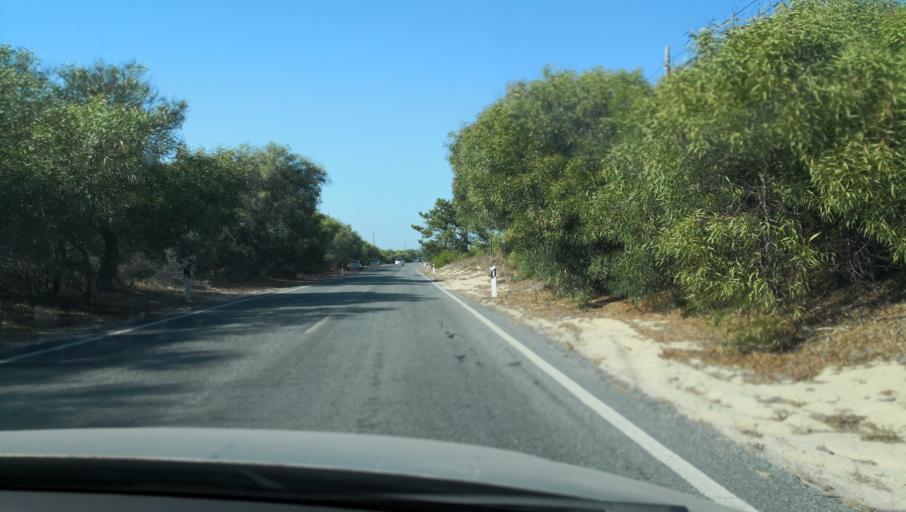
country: PT
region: Setubal
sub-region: Setubal
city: Setubal
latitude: 38.3956
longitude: -8.8044
